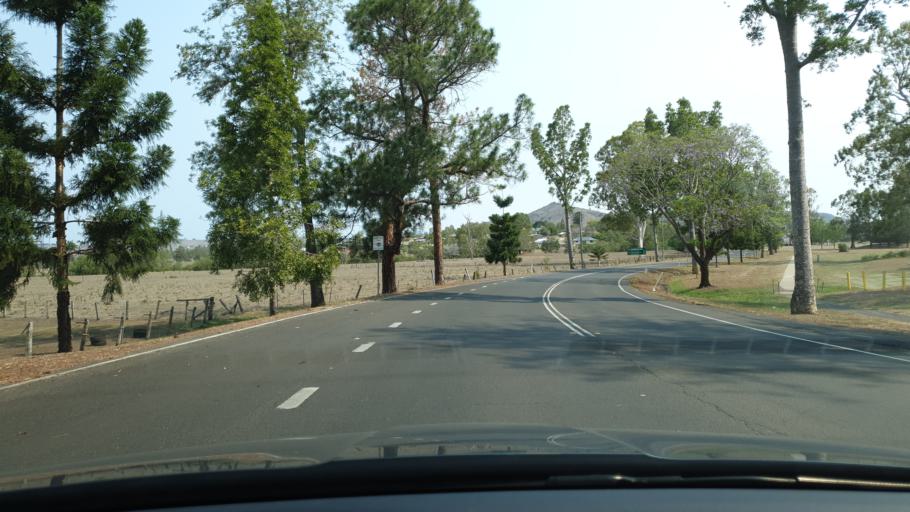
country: AU
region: Queensland
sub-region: Ipswich
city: Deebing Heights
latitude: -28.0005
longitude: 152.6819
